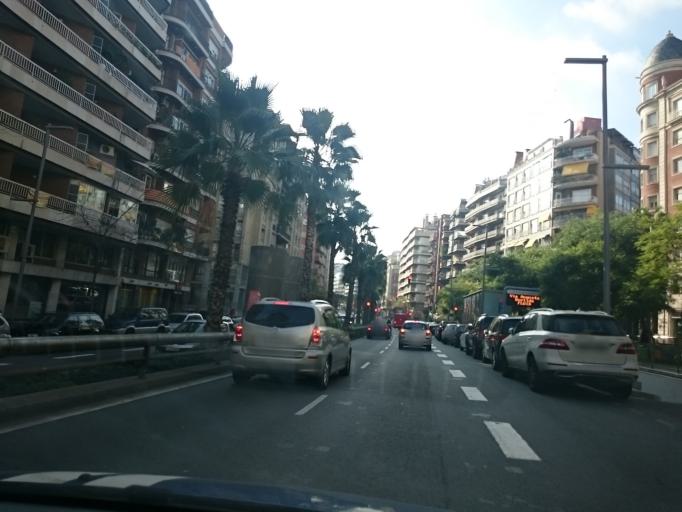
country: ES
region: Catalonia
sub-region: Provincia de Barcelona
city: Sarria-Sant Gervasi
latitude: 41.4053
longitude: 2.1431
